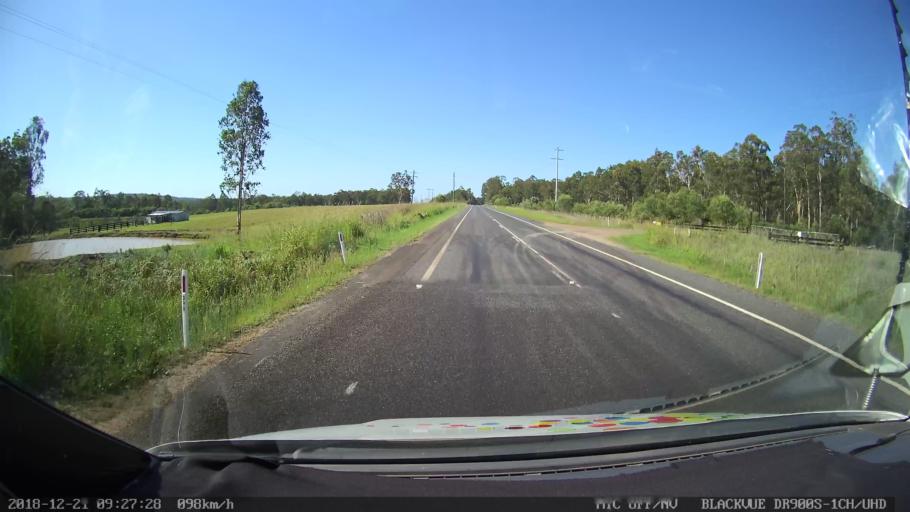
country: AU
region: New South Wales
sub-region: Clarence Valley
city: Maclean
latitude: -29.4033
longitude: 152.9899
